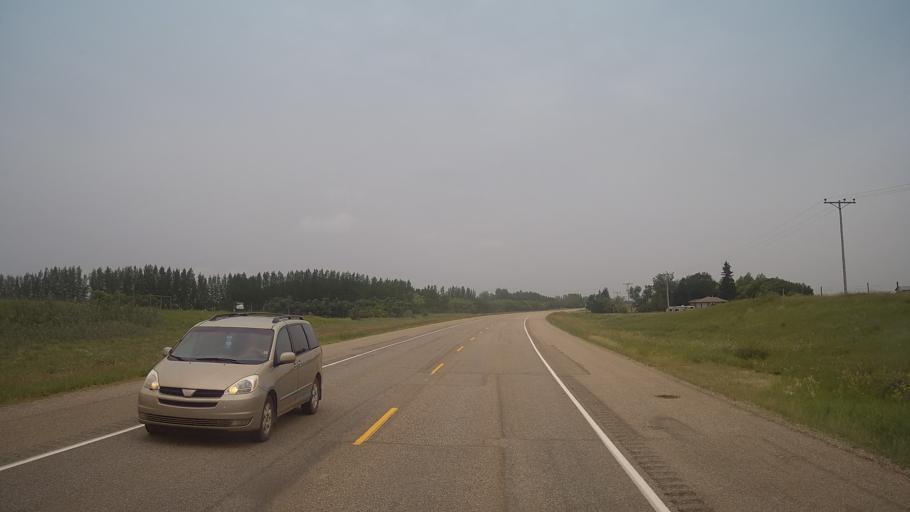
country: CA
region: Saskatchewan
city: Biggar
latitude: 52.0569
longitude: -107.9017
